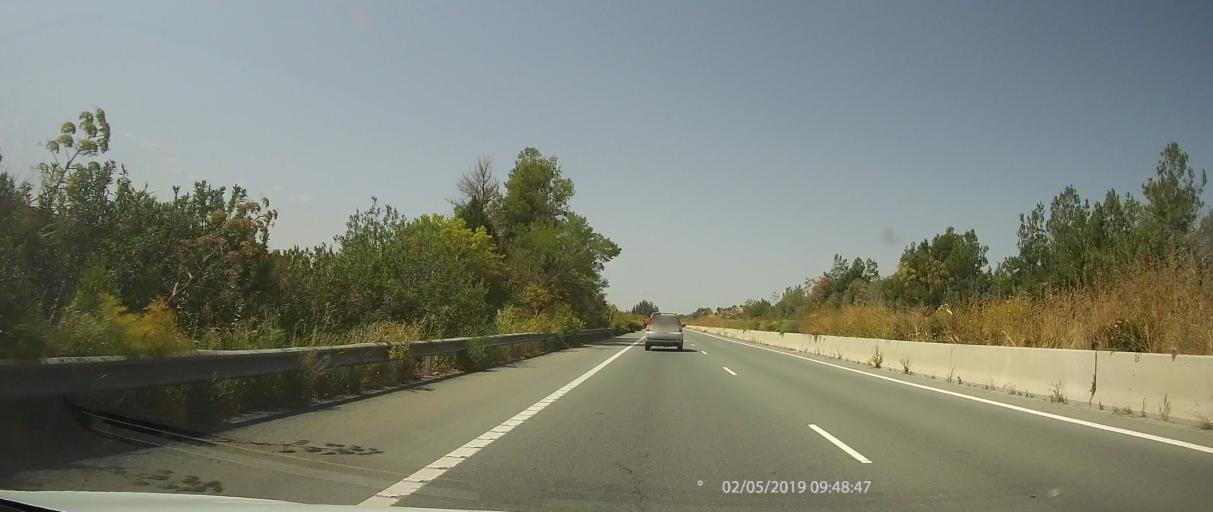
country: CY
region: Larnaka
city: Tersefanou
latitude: 34.8822
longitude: 33.5151
